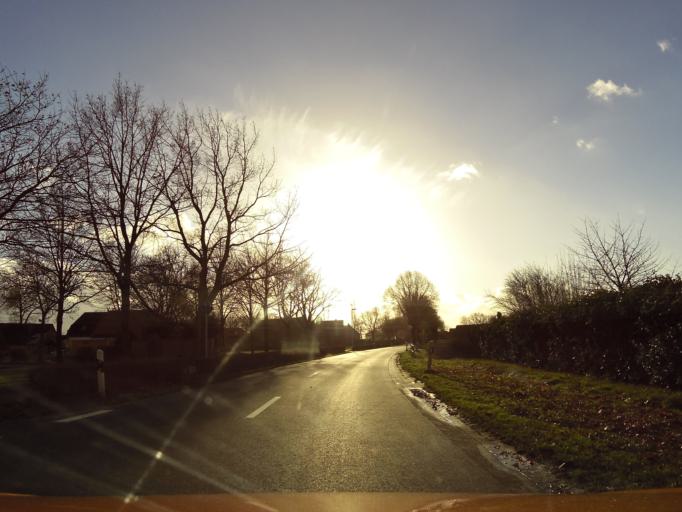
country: DE
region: Lower Saxony
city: Langwedel
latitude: 52.9547
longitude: 9.1923
